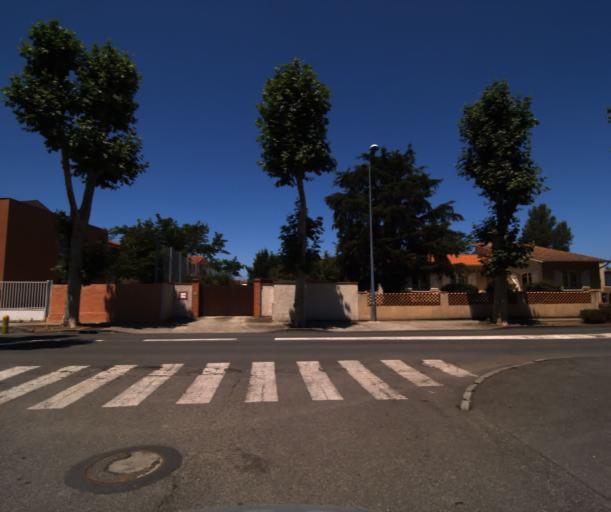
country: FR
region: Midi-Pyrenees
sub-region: Departement de la Haute-Garonne
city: Muret
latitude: 43.4616
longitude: 1.3196
